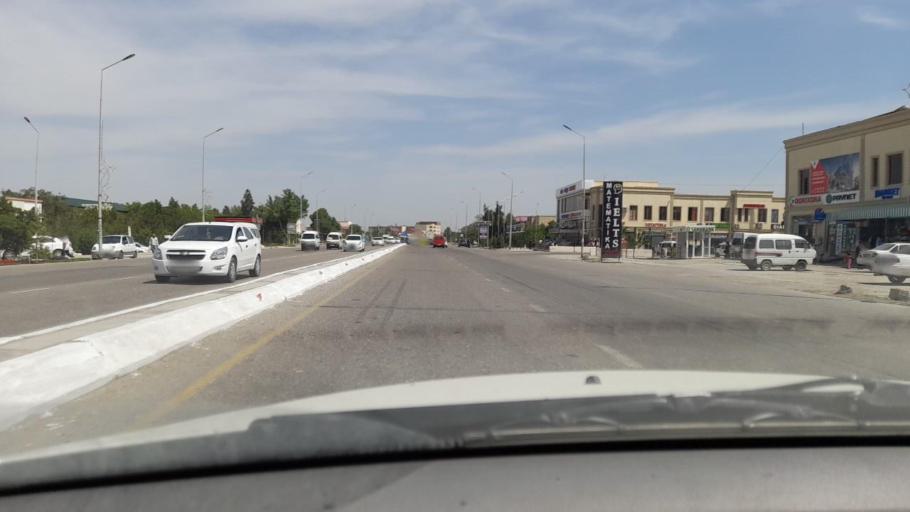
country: UZ
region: Bukhara
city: Galaosiyo
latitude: 39.8581
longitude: 64.4425
